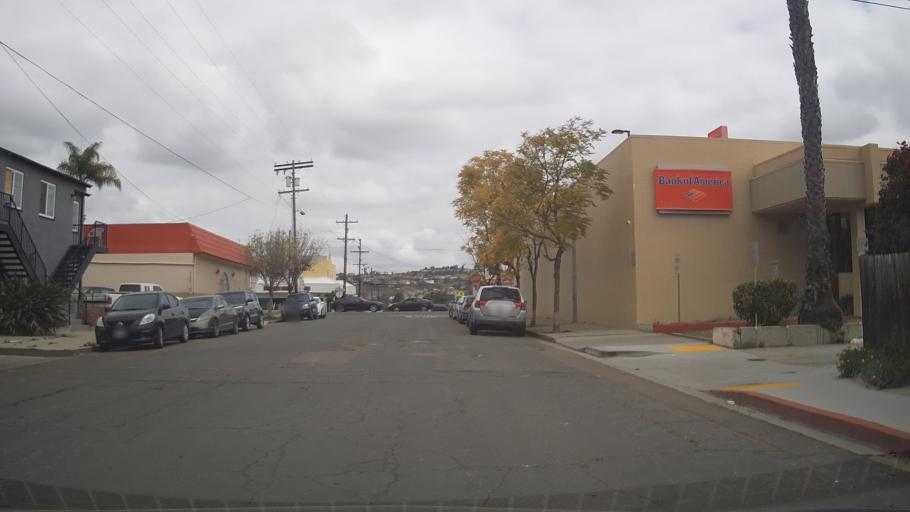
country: US
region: California
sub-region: San Diego County
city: La Mesa
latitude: 32.7680
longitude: -117.0514
